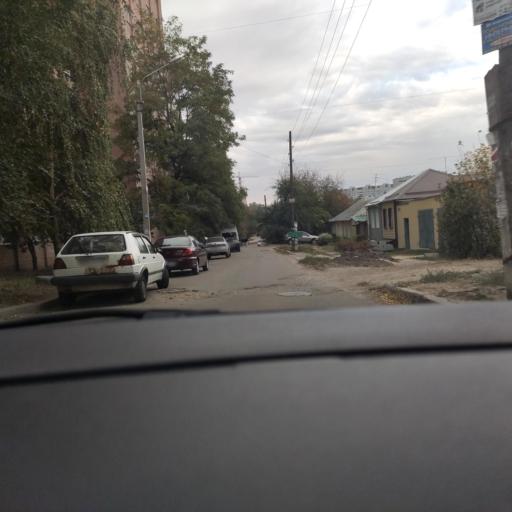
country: RU
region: Voronezj
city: Voronezh
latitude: 51.6891
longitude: 39.1992
